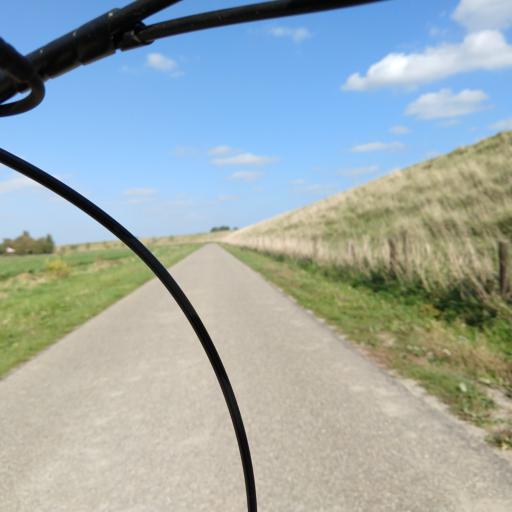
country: NL
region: Zeeland
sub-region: Gemeente Goes
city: Goes
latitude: 51.5511
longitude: 3.8690
